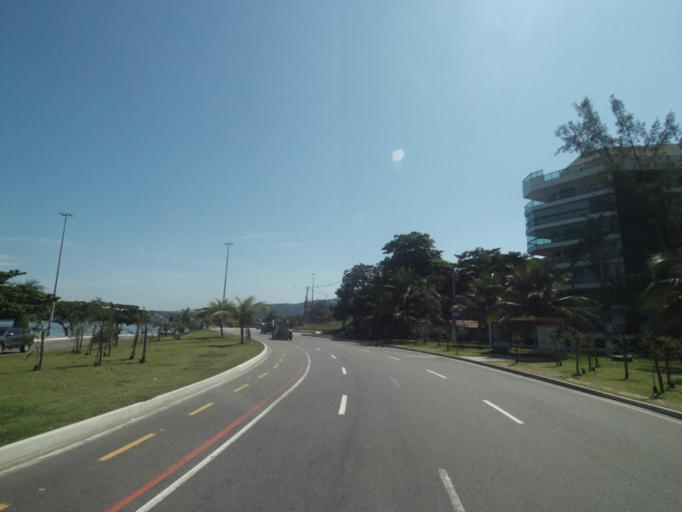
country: BR
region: Rio de Janeiro
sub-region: Niteroi
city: Niteroi
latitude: -22.9311
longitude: -43.0976
